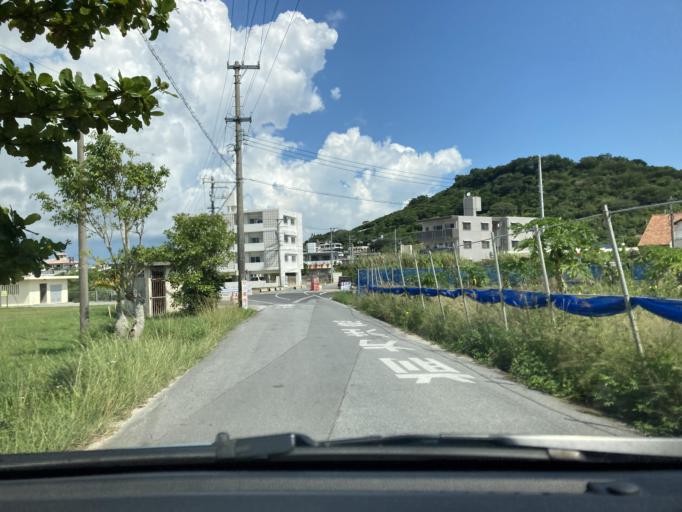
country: JP
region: Okinawa
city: Tomigusuku
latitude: 26.1618
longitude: 127.7567
